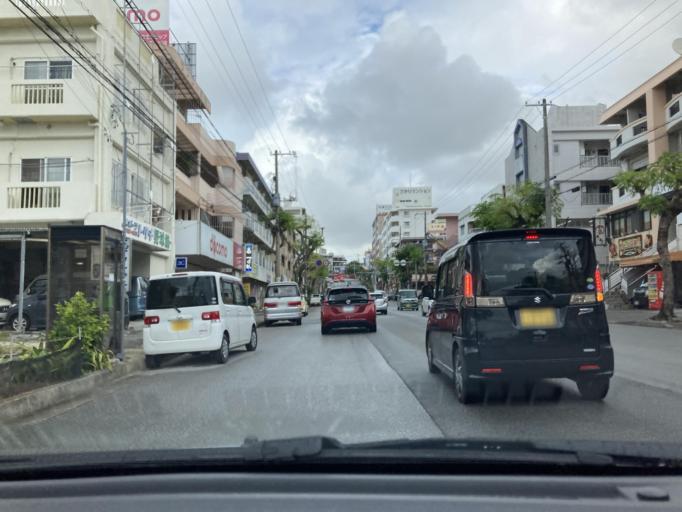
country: JP
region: Okinawa
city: Tomigusuku
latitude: 26.1976
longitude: 127.6962
